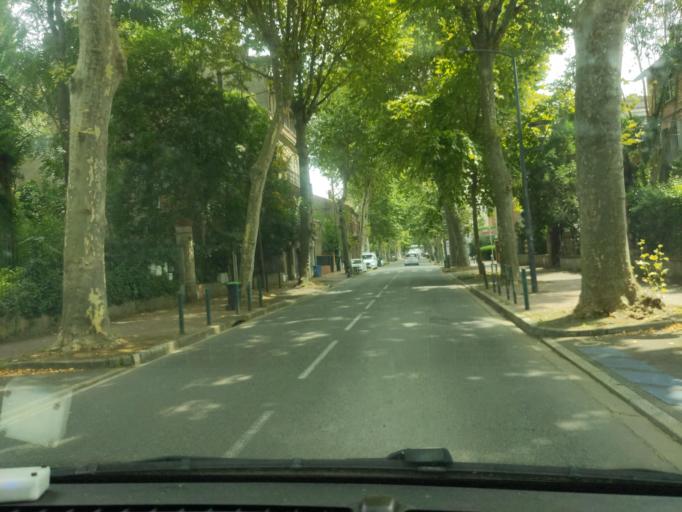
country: FR
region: Midi-Pyrenees
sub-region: Departement de la Haute-Garonne
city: Toulouse
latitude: 43.5900
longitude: 1.4547
